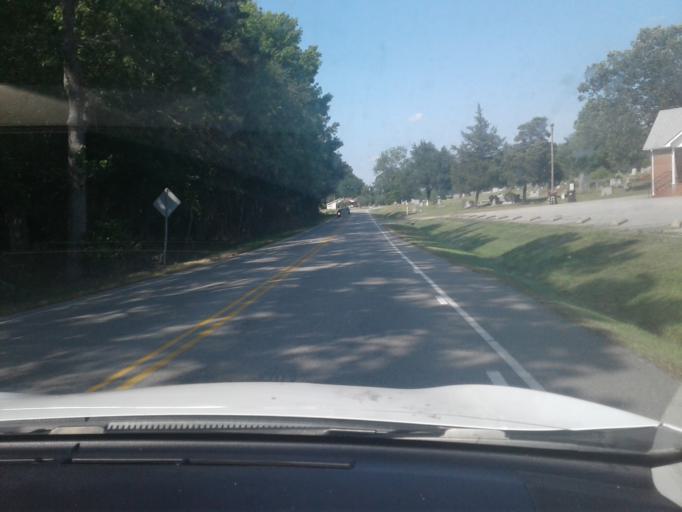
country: US
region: North Carolina
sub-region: Harnett County
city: Erwin
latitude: 35.3315
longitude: -78.6571
